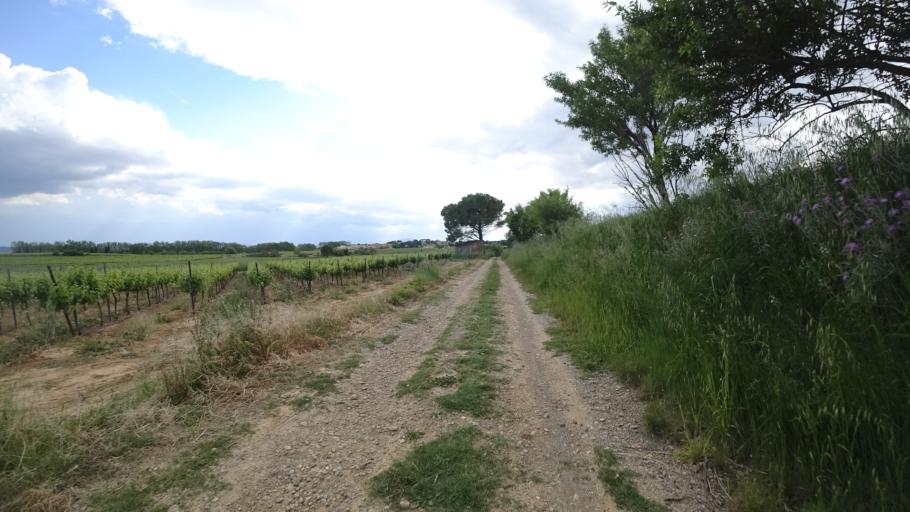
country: FR
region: Languedoc-Roussillon
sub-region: Departement de l'Aude
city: Ginestas
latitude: 43.2531
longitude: 2.8744
